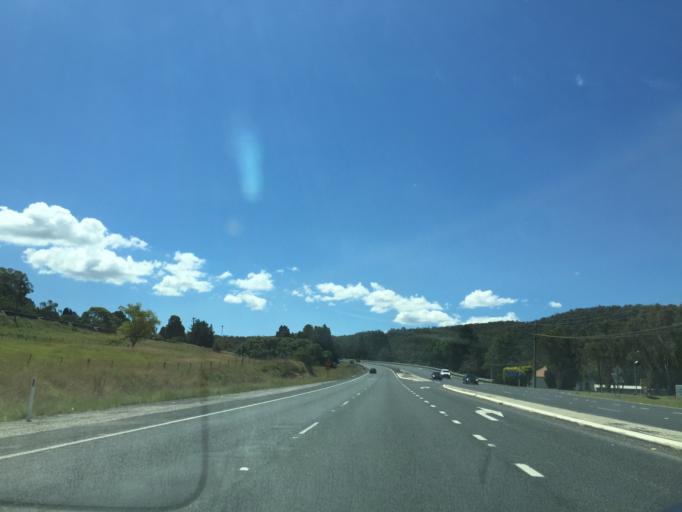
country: AU
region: New South Wales
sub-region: Lithgow
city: Lithgow
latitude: -33.4360
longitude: 150.1129
